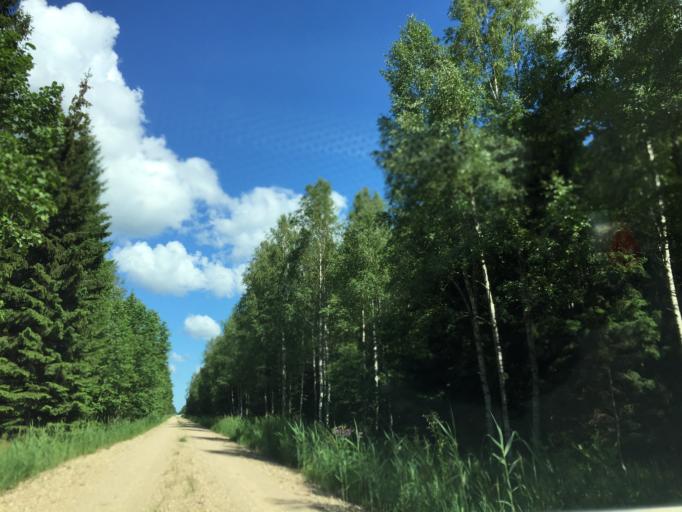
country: LV
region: Ventspils Rajons
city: Piltene
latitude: 57.2836
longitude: 21.8510
